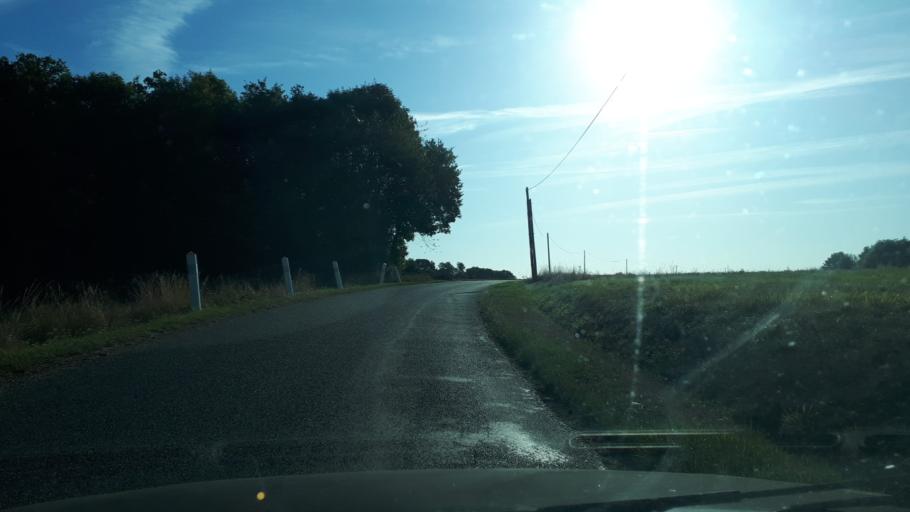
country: FR
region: Centre
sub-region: Departement d'Indre-et-Loire
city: Chateau-Renault
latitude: 47.6604
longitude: 0.9365
